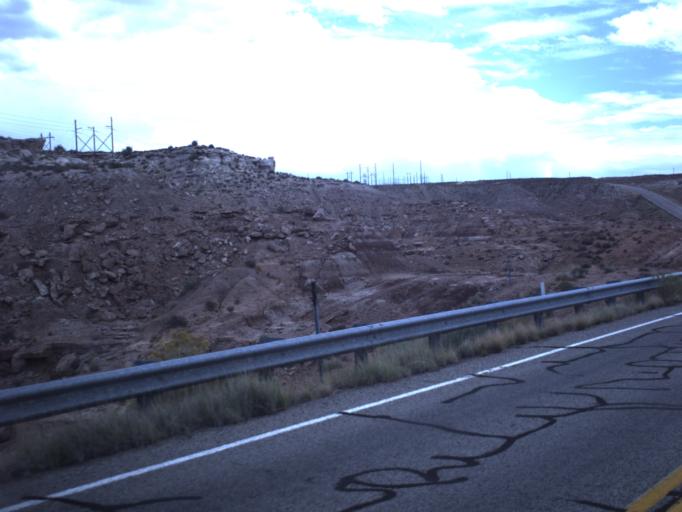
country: US
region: Utah
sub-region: San Juan County
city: Blanding
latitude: 37.2846
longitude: -109.3855
